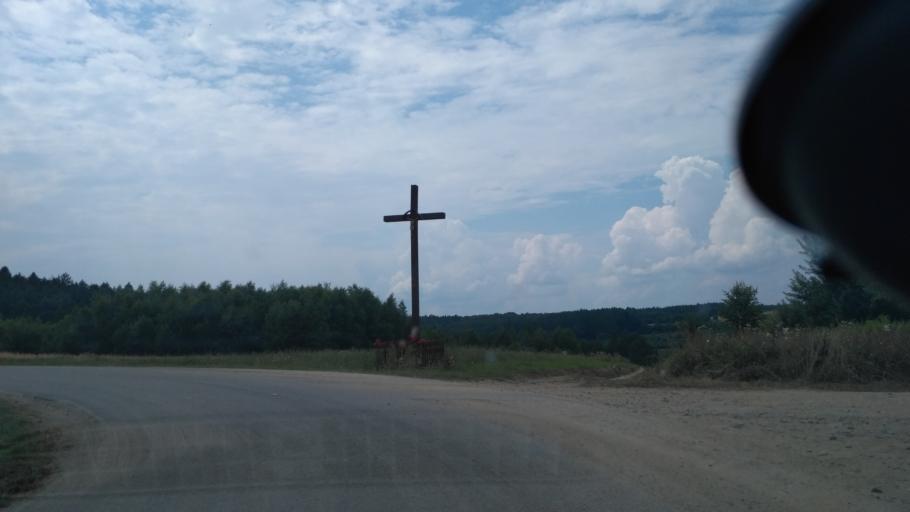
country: PL
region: Subcarpathian Voivodeship
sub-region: Powiat przeworski
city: Lopuszka Wielka
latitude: 49.9119
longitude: 22.3966
